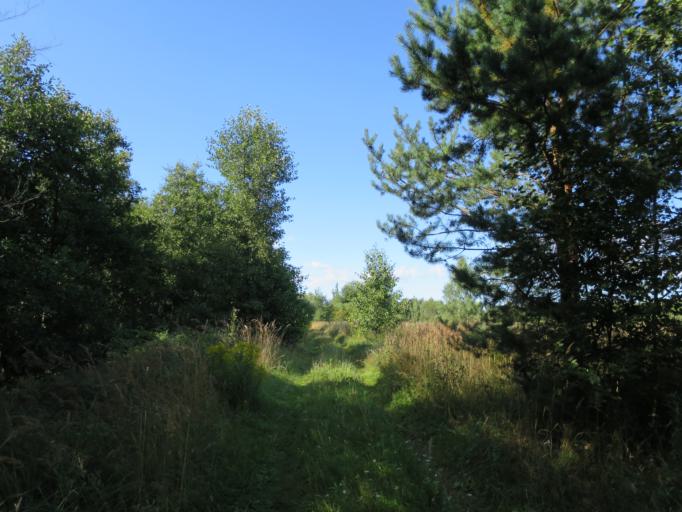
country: LV
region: Riga
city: Jaunciems
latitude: 57.0755
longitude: 24.2164
